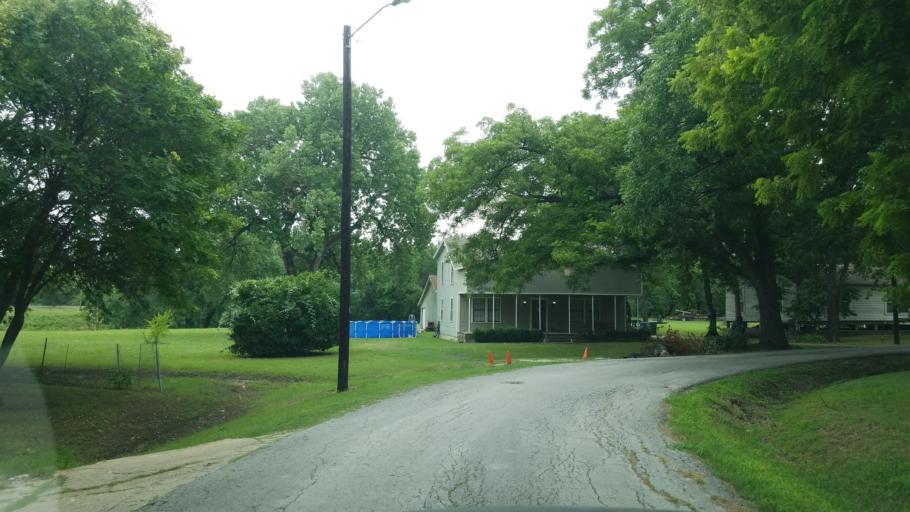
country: US
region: Texas
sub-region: Dallas County
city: Cockrell Hill
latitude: 32.7915
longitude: -96.8927
